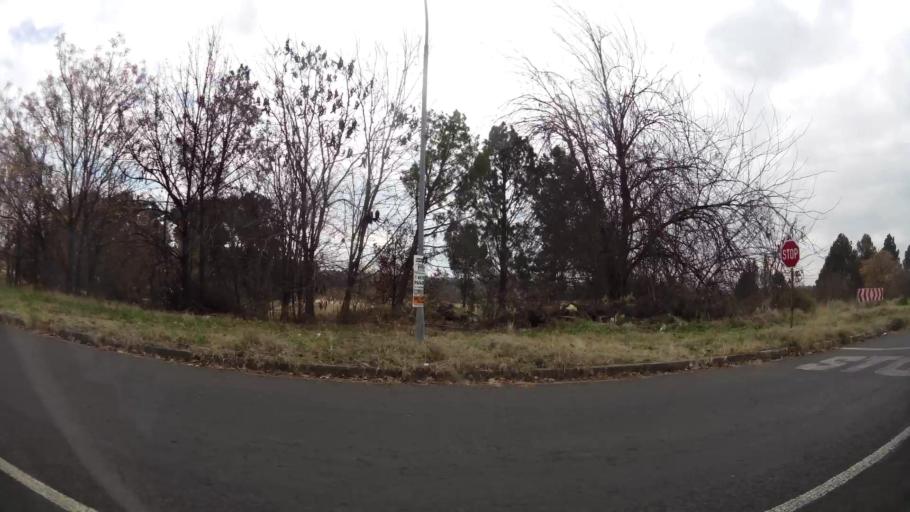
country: ZA
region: Orange Free State
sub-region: Fezile Dabi District Municipality
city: Kroonstad
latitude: -27.6687
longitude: 27.2482
